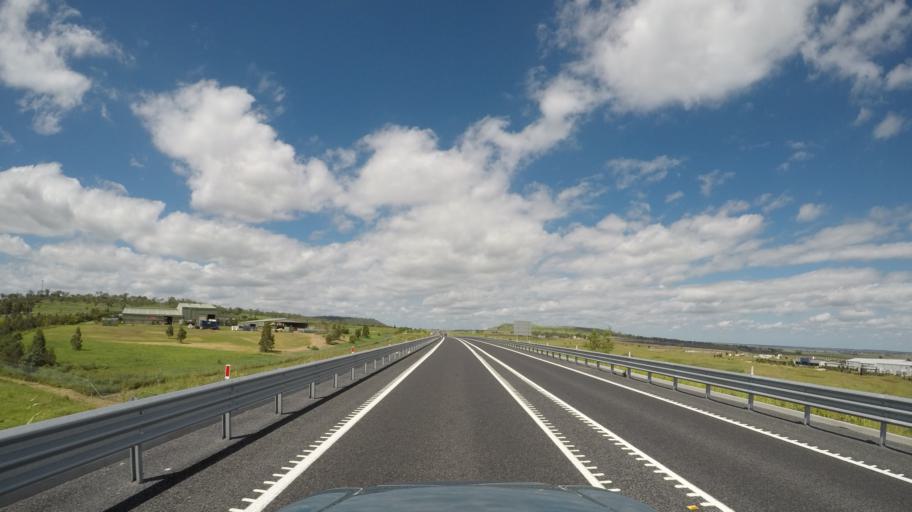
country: AU
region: Queensland
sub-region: Toowoomba
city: Wilsonton Heights
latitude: -27.5392
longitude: 151.8442
